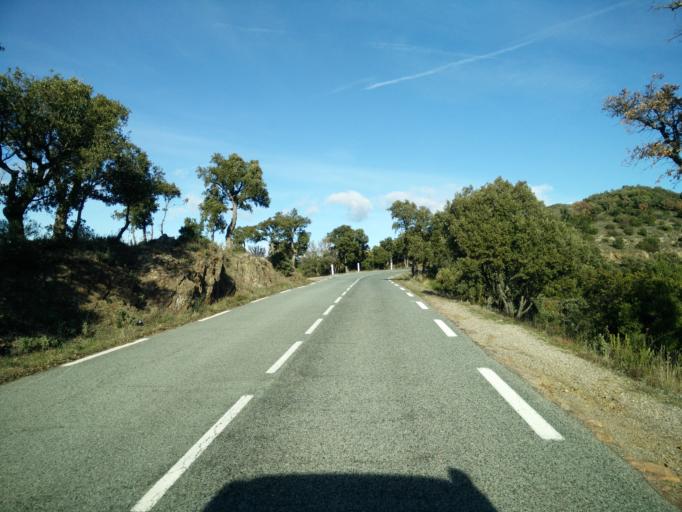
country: FR
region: Provence-Alpes-Cote d'Azur
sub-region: Departement du Var
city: Saint-Raphael
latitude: 43.4937
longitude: 6.7786
